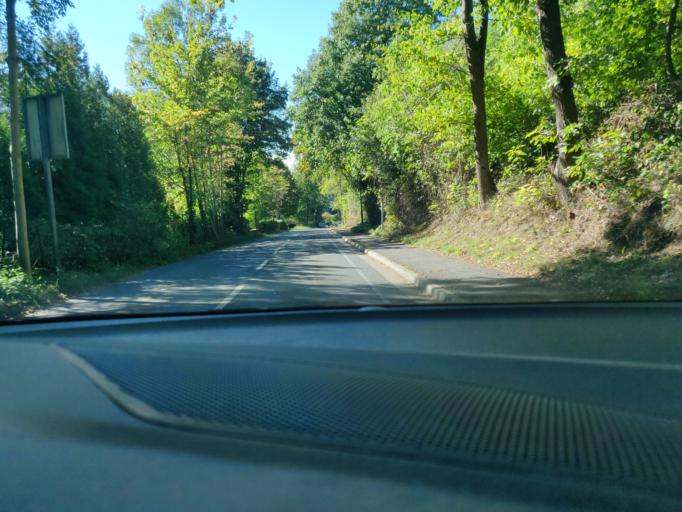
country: DE
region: North Rhine-Westphalia
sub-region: Regierungsbezirk Dusseldorf
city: Heiligenhaus
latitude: 51.3541
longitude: 6.9415
